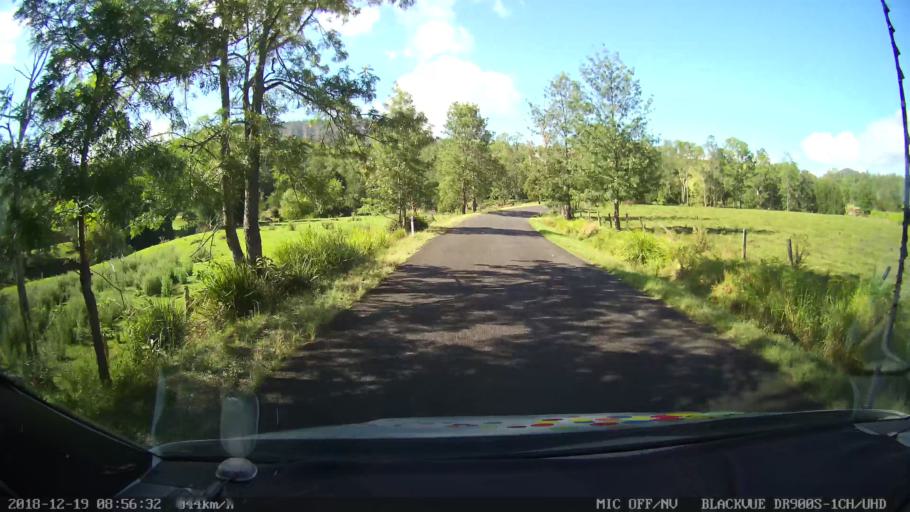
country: AU
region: New South Wales
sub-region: Kyogle
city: Kyogle
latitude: -28.4194
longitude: 152.9764
